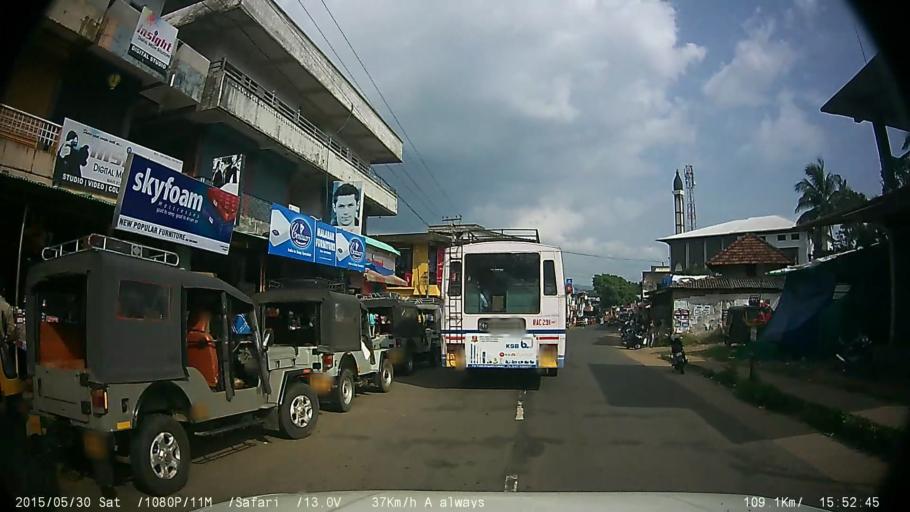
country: IN
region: Kerala
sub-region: Wayanad
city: Panamaram
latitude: 11.6766
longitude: 76.0756
